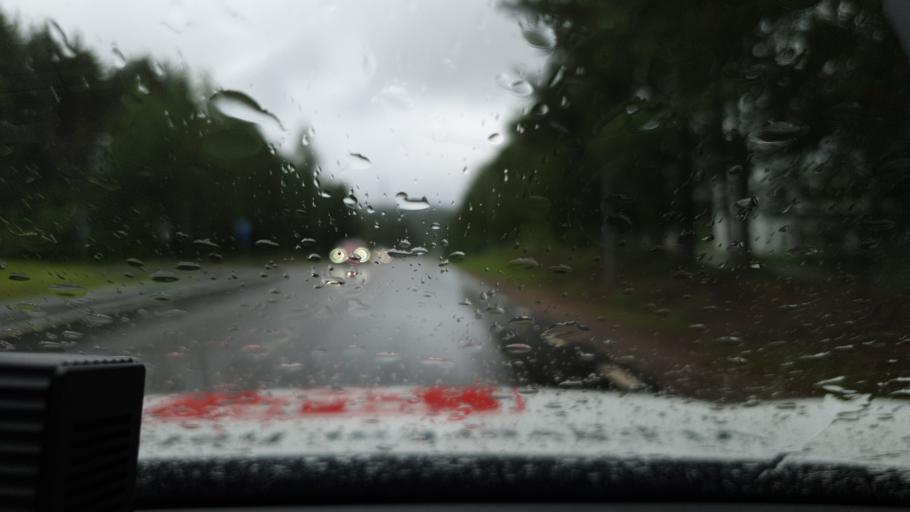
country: SE
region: Norrbotten
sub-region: Jokkmokks Kommun
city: Jokkmokk
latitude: 66.6063
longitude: 19.8228
